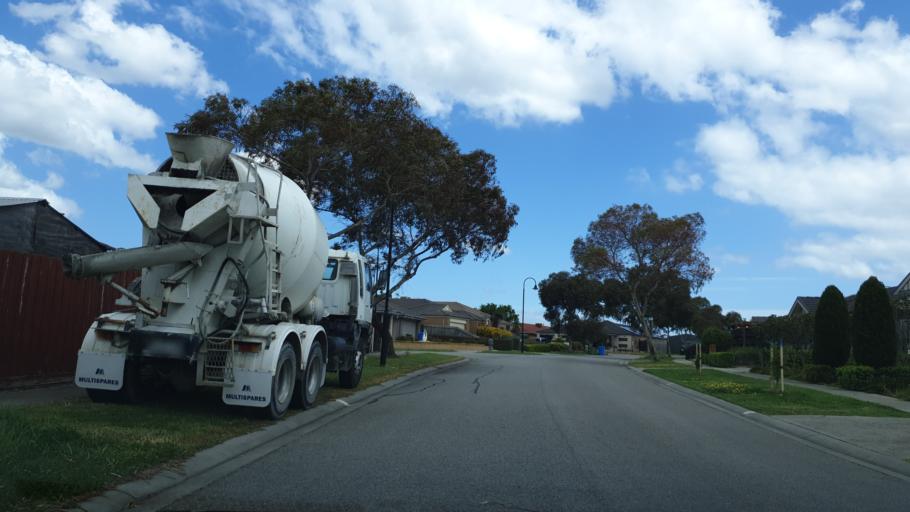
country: AU
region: Victoria
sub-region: Casey
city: Cranbourne
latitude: -38.0930
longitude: 145.2857
